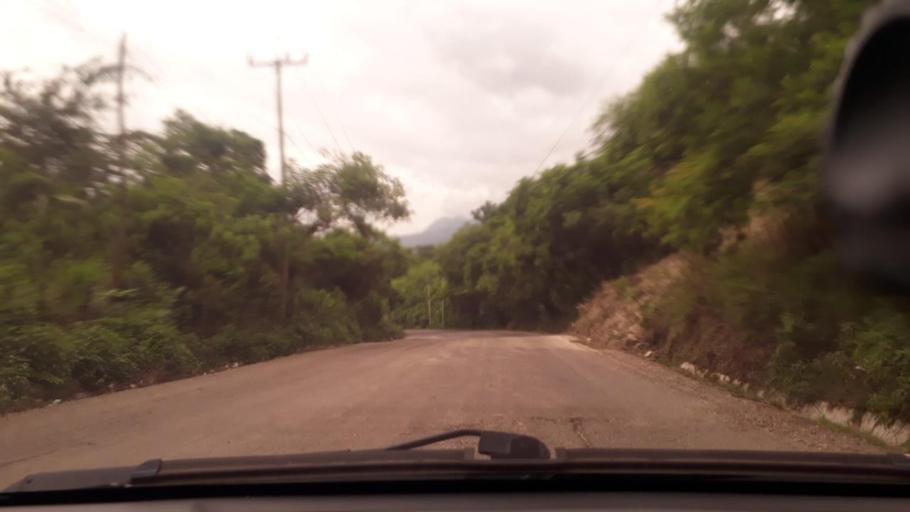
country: GT
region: Chiquimula
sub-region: Municipio de San Juan Ermita
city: San Juan Ermita
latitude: 14.7480
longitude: -89.4538
